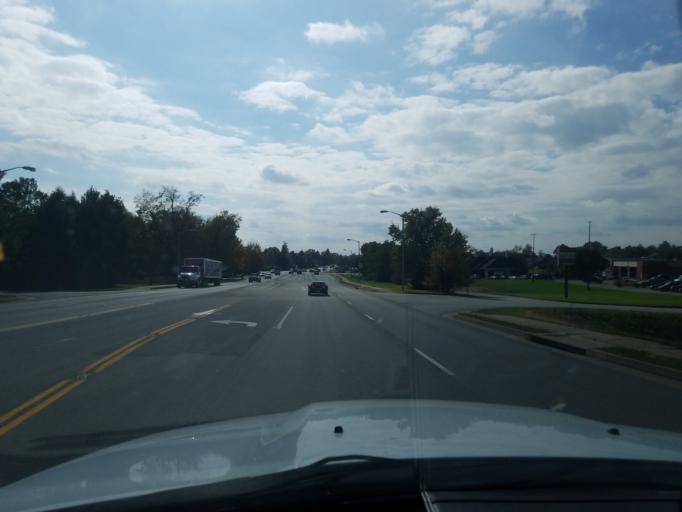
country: US
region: Kentucky
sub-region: Nelson County
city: Bardstown
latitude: 37.8281
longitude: -85.4615
